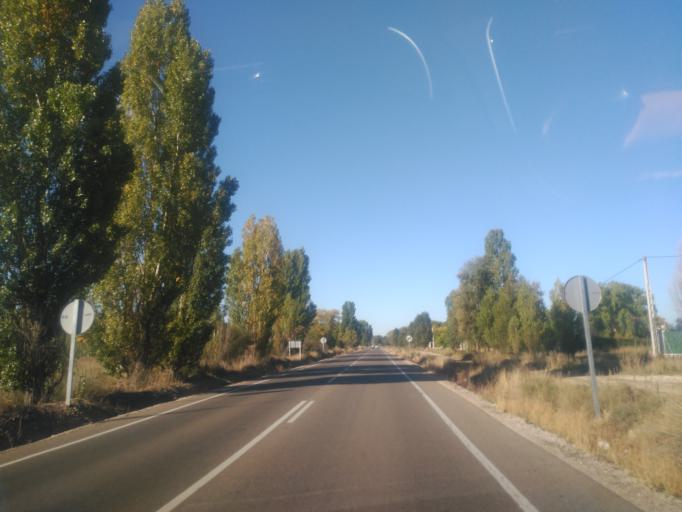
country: ES
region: Castille and Leon
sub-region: Provincia de Burgos
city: Fresnillo de las Duenas
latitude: 41.6814
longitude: -3.6353
